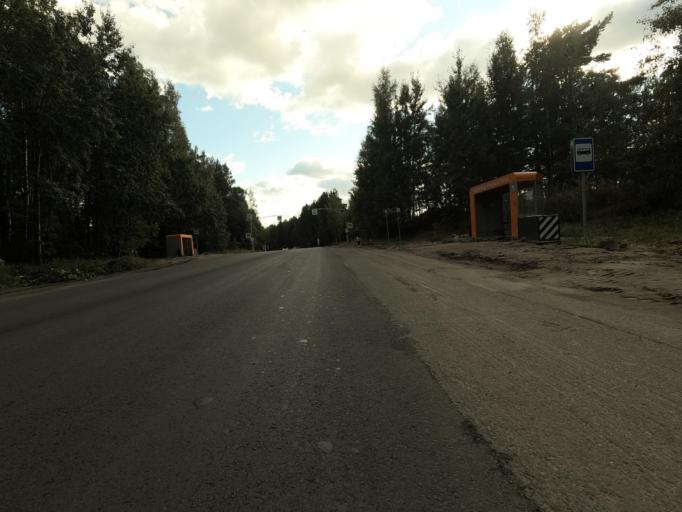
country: RU
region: Leningrad
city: Koltushi
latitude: 59.9547
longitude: 30.6572
